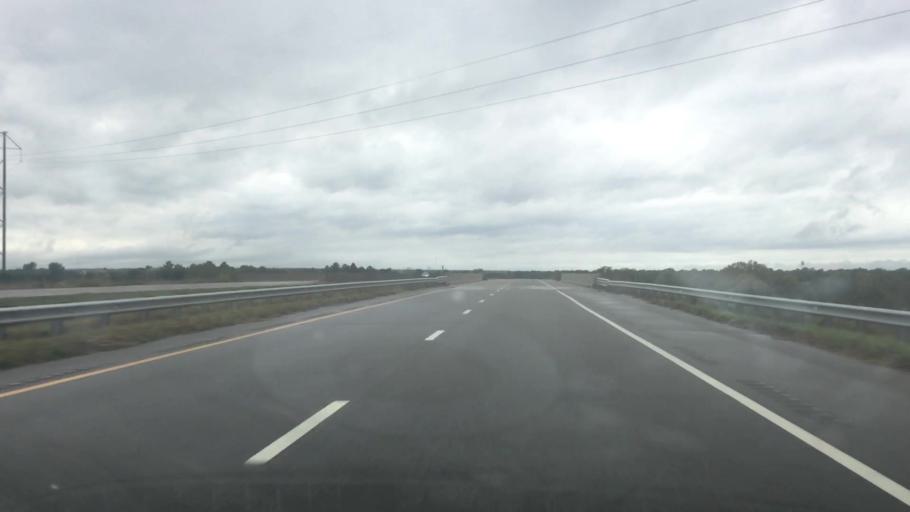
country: US
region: Kansas
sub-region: Miami County
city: Osawatomie
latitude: 38.5226
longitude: -94.9067
